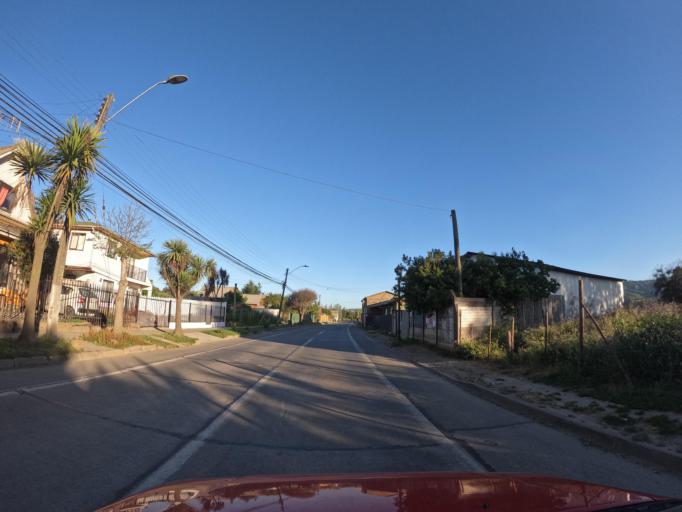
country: CL
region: Maule
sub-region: Provincia de Talca
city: Talca
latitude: -34.9896
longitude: -71.9817
